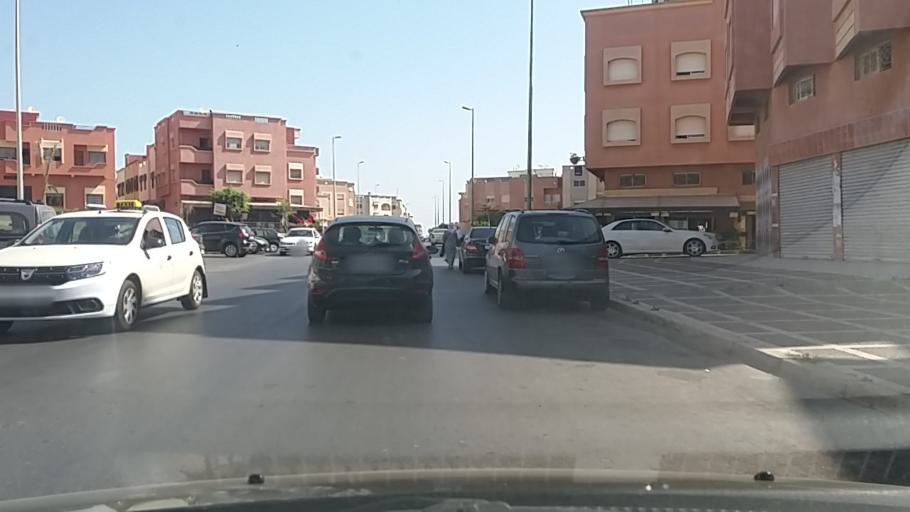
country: MA
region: Gharb-Chrarda-Beni Hssen
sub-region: Kenitra Province
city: Kenitra
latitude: 34.2701
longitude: -6.6107
